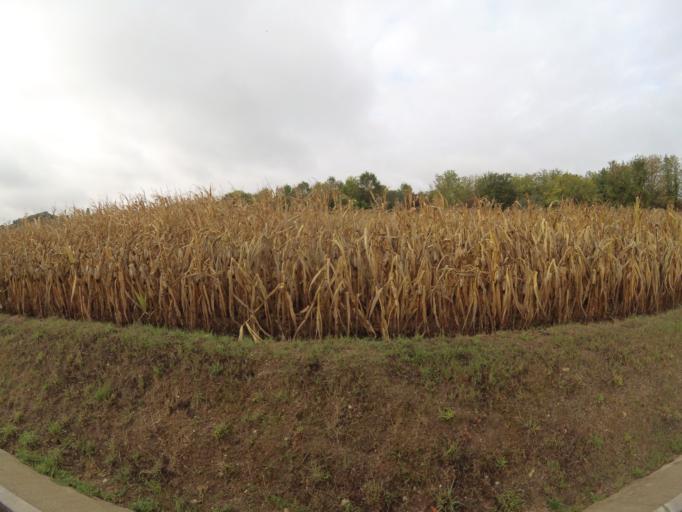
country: FR
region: Ile-de-France
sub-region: Departement de Seine-et-Marne
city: Dampmart
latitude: 48.8765
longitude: 2.7331
